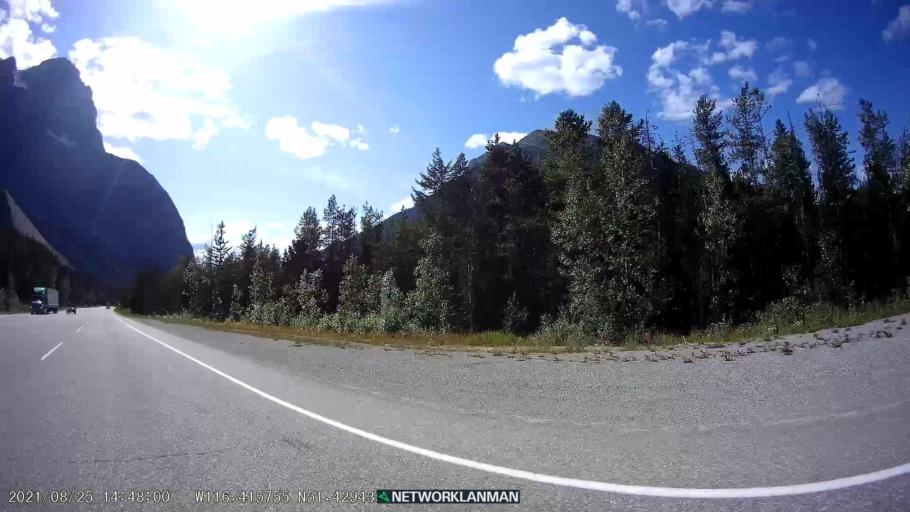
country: CA
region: Alberta
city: Lake Louise
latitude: 51.4295
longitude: -116.4160
